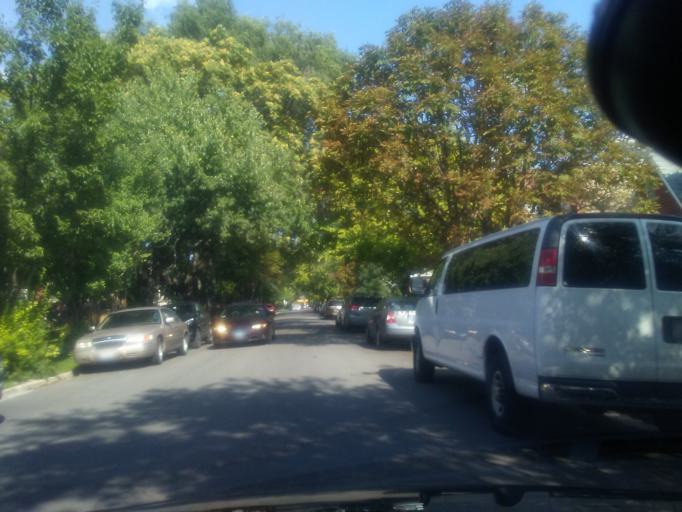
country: US
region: Illinois
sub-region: Cook County
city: Lincolnwood
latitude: 41.9734
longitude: -87.7570
